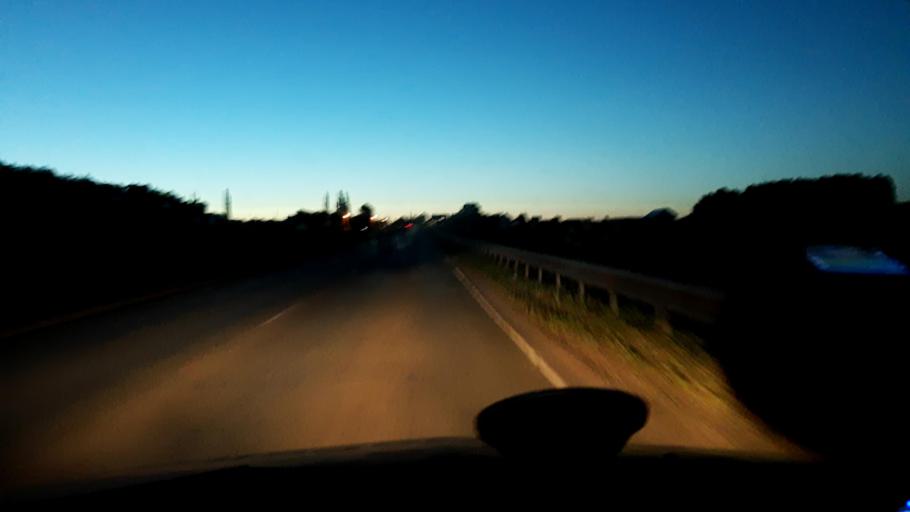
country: RU
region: Bashkortostan
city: Chishmy
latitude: 54.6255
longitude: 55.3764
